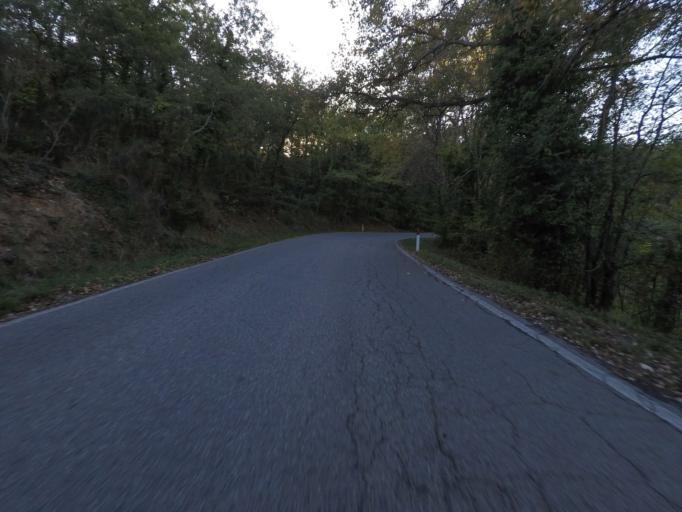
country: IT
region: Tuscany
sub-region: Provincia di Siena
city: Radda in Chianti
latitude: 43.4780
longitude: 11.3704
